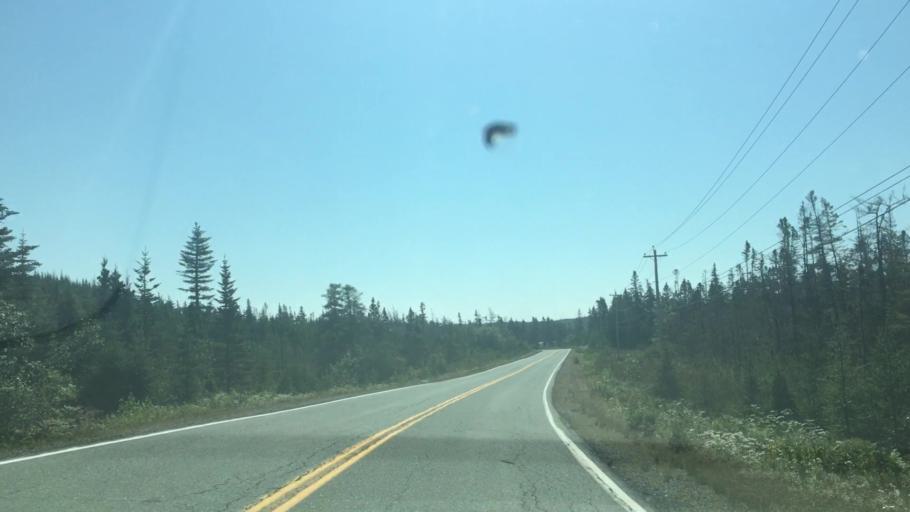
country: CA
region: Nova Scotia
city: Antigonish
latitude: 45.0104
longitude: -62.0909
